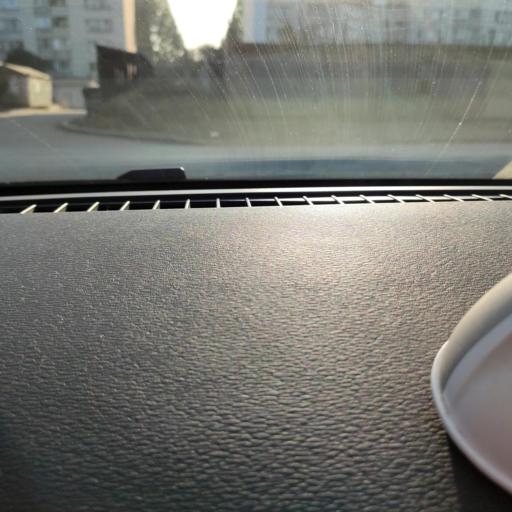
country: RU
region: Samara
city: Petra-Dubrava
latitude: 53.2362
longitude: 50.2859
